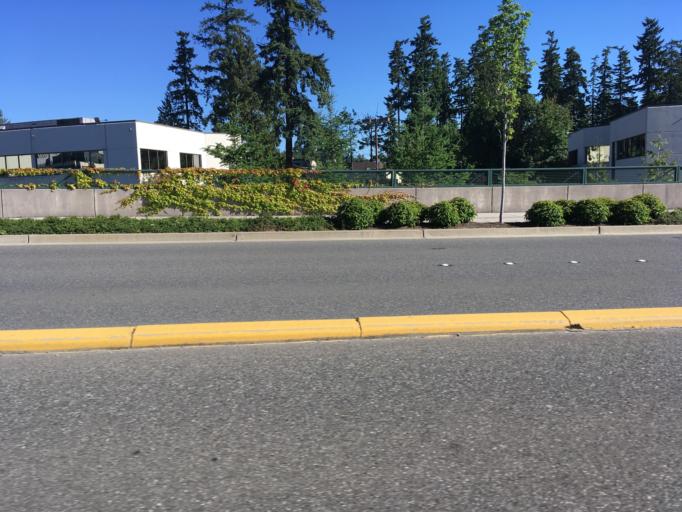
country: US
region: Washington
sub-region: King County
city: Bellevue
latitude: 47.6225
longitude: -122.1871
